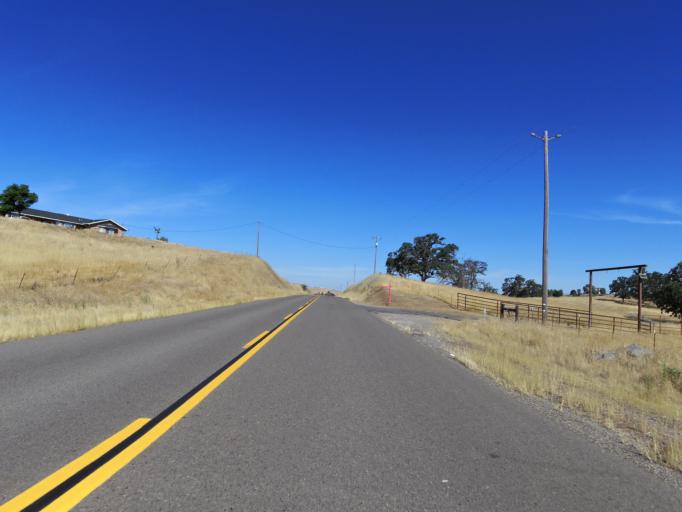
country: US
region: California
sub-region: Madera County
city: Bonadelle Ranchos-Madera Ranchos
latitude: 37.1082
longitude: -119.9046
